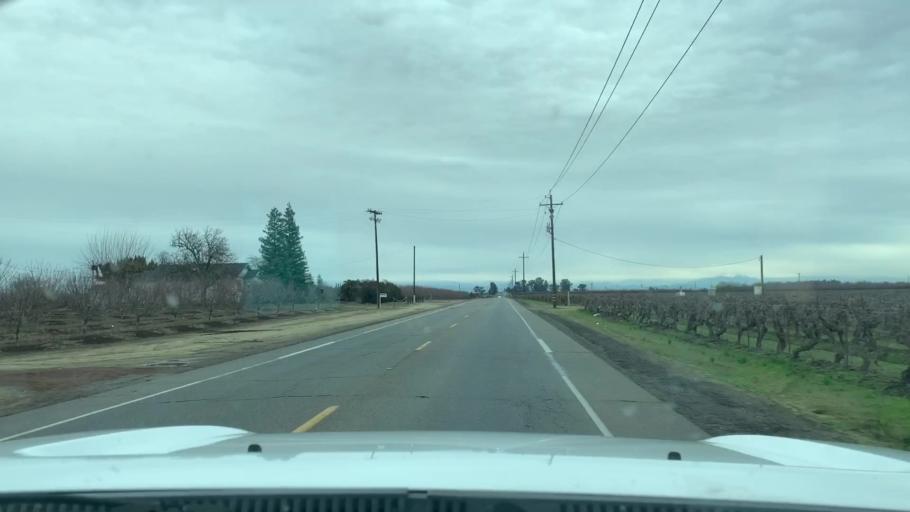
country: US
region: California
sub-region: Fresno County
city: Fowler
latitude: 36.6054
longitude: -119.6780
